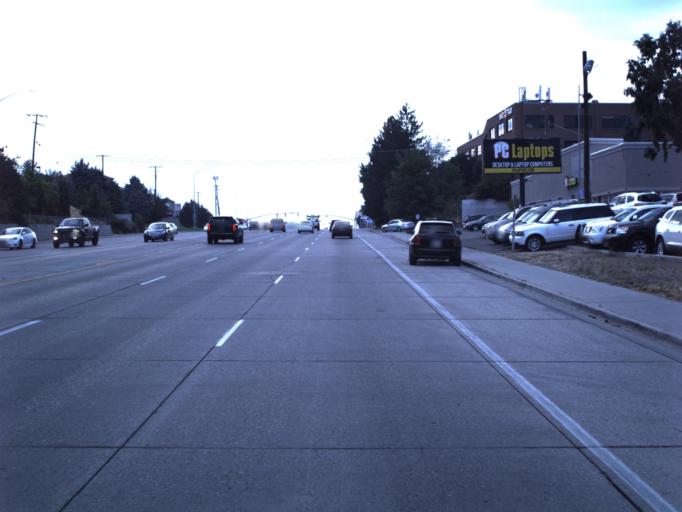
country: US
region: Utah
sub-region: Utah County
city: Provo
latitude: 40.2624
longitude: -111.6778
